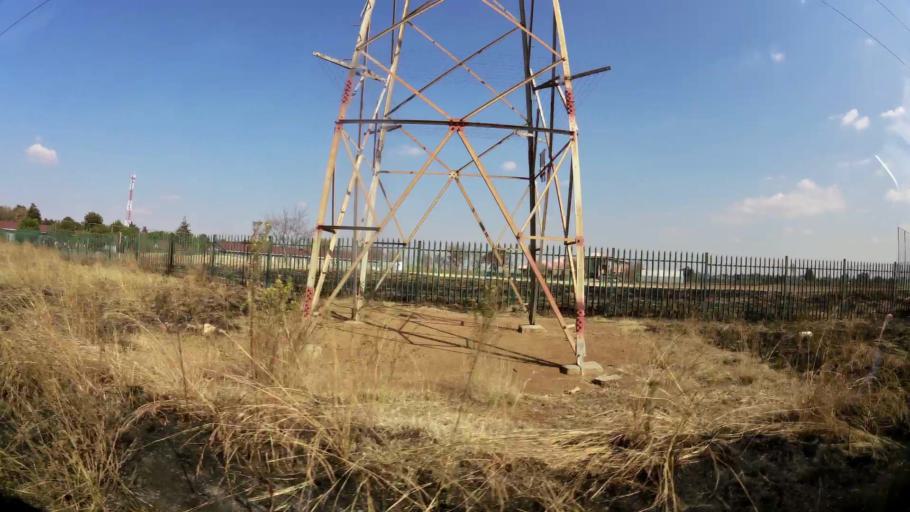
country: ZA
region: Gauteng
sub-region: Ekurhuleni Metropolitan Municipality
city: Benoni
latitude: -26.1415
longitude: 28.3980
